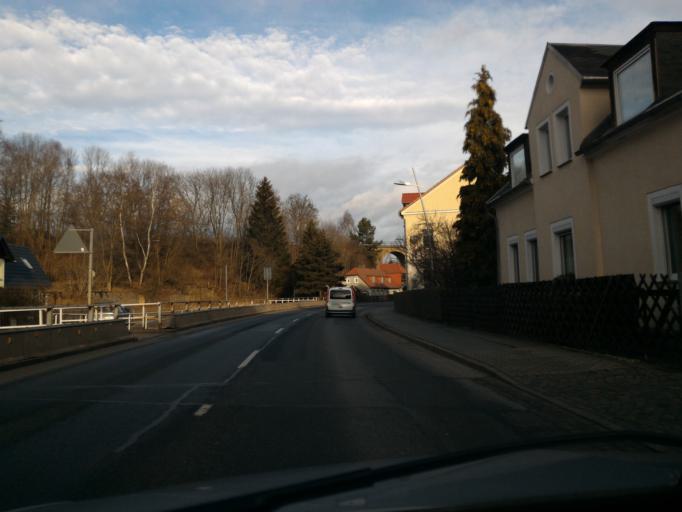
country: DE
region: Saxony
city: Ebersbach
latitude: 51.0099
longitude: 14.5818
